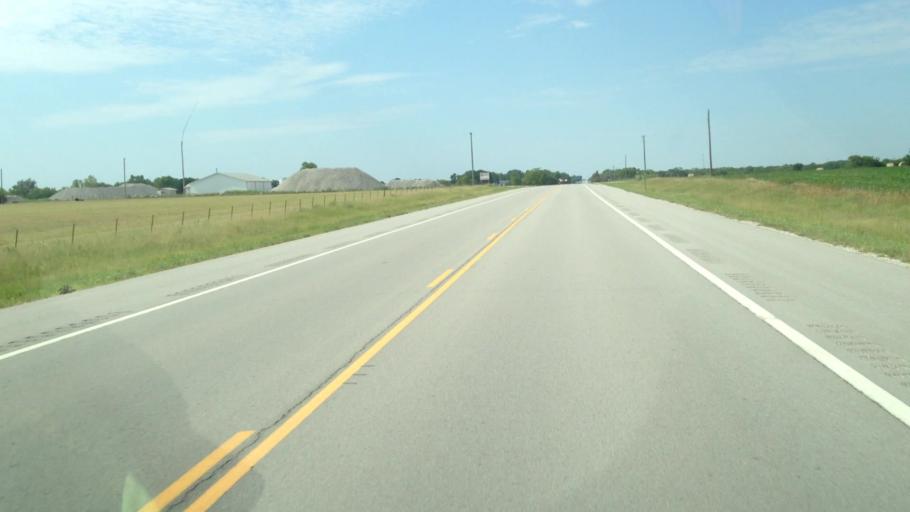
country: US
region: Kansas
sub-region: Labette County
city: Parsons
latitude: 37.2794
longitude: -95.2675
